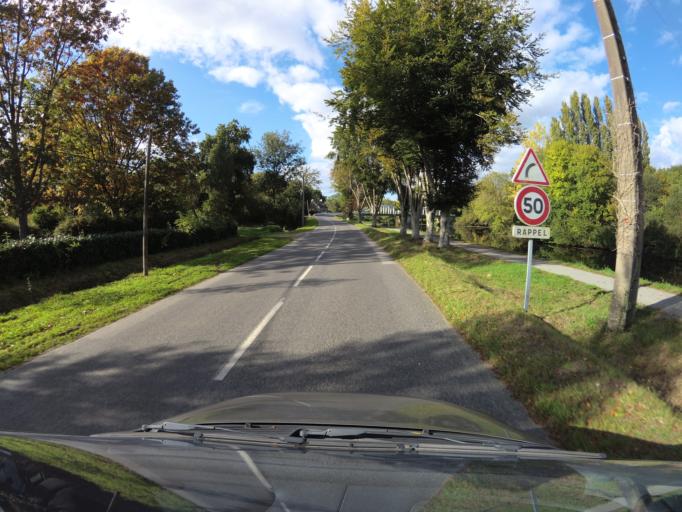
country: FR
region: Brittany
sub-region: Departement du Morbihan
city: Peillac
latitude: 47.7277
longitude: -2.2137
